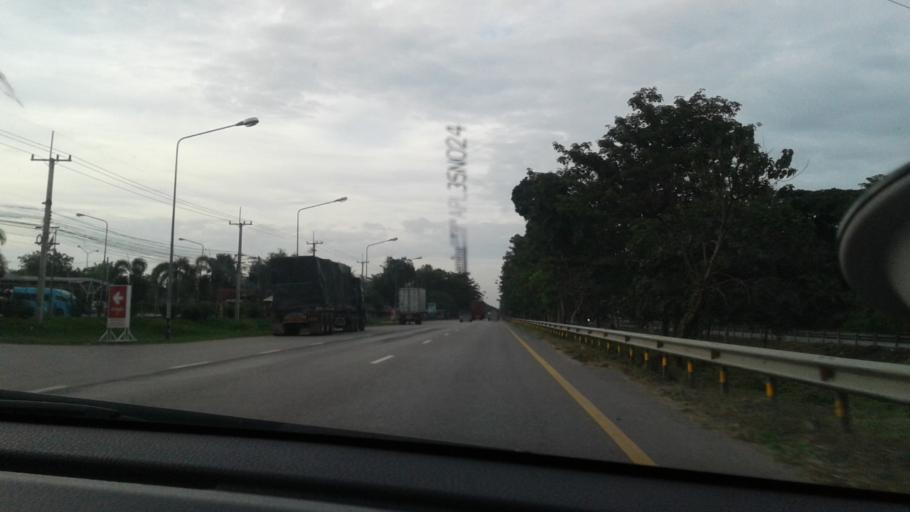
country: TH
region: Prachuap Khiri Khan
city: Pran Buri
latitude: 12.4236
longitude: 99.9214
